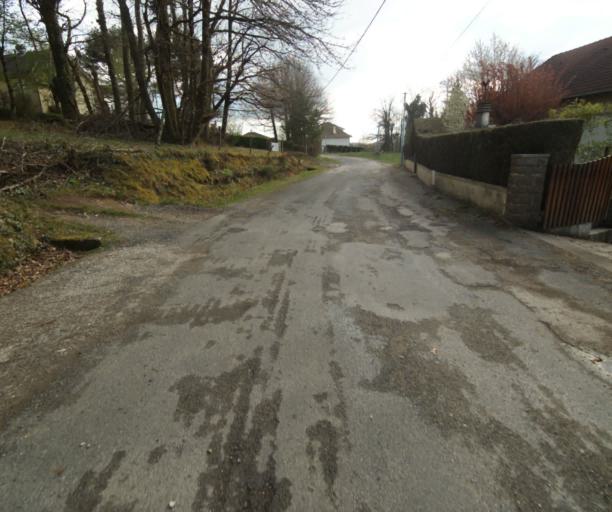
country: FR
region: Limousin
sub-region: Departement de la Correze
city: Tulle
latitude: 45.2526
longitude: 1.7454
